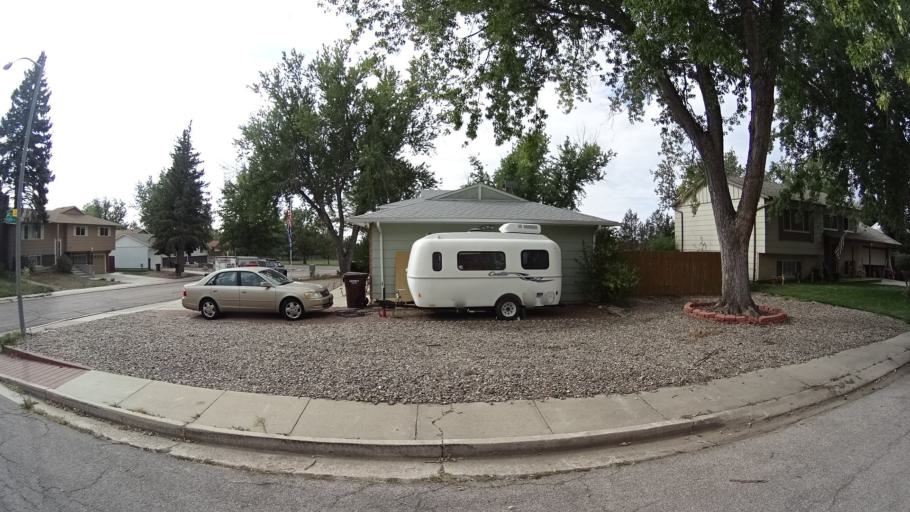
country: US
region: Colorado
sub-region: El Paso County
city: Cimarron Hills
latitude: 38.8552
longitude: -104.7452
